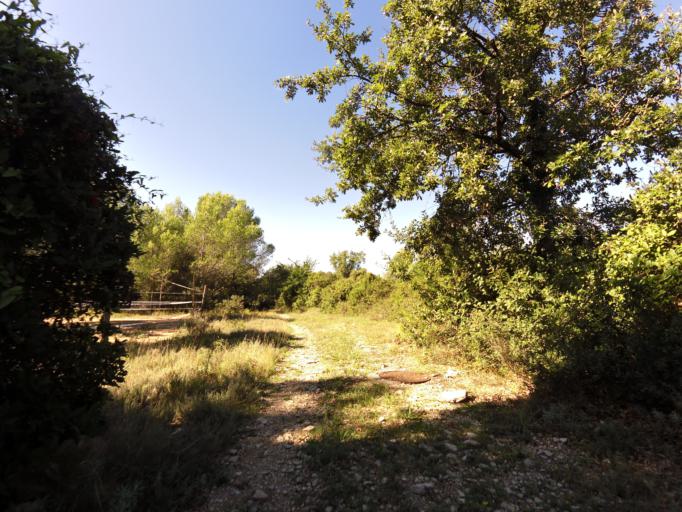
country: FR
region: Languedoc-Roussillon
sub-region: Departement de l'Herault
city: Villetelle
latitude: 43.7423
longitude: 4.1361
